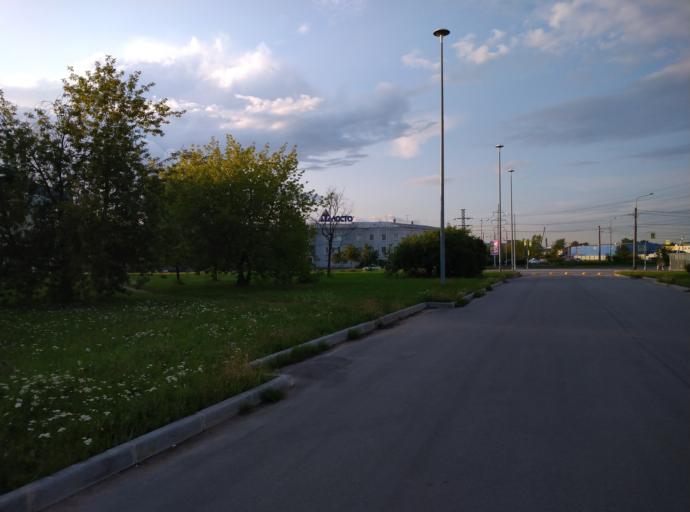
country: RU
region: St.-Petersburg
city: Kupchino
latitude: 59.8710
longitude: 30.3432
